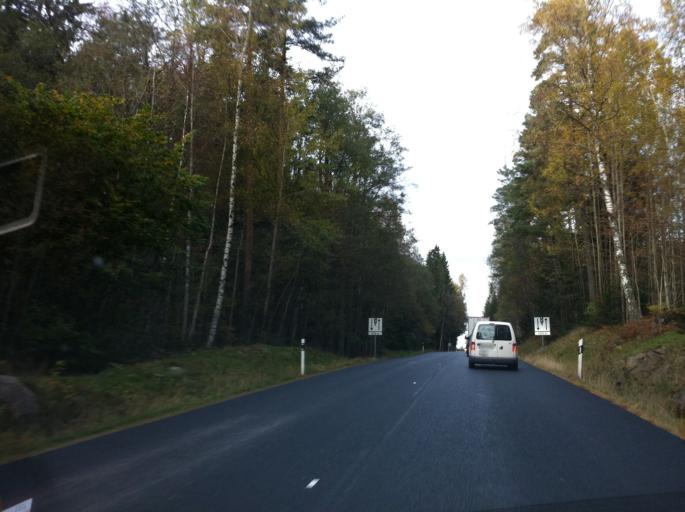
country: SE
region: OEstergoetland
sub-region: Motala Kommun
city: Ryd
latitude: 58.7563
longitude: 14.9909
